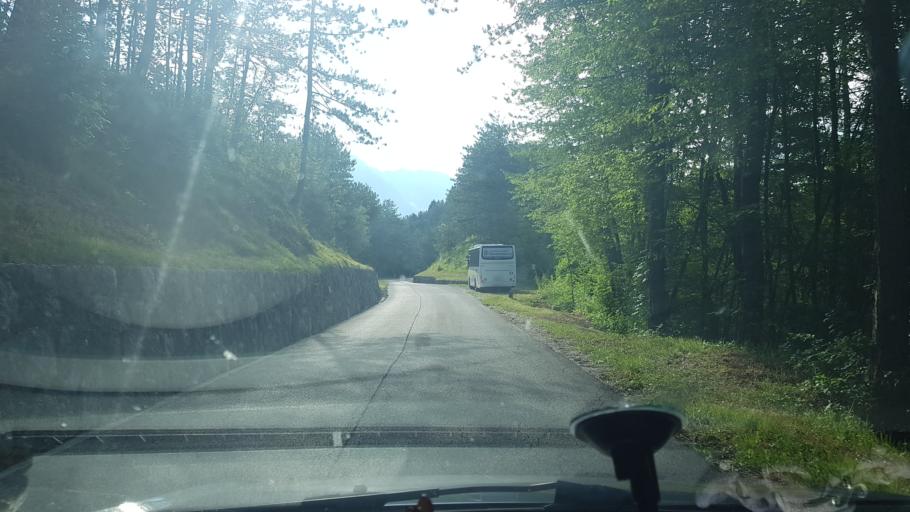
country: IT
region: Friuli Venezia Giulia
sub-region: Provincia di Udine
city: Prato
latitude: 46.3645
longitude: 13.3327
